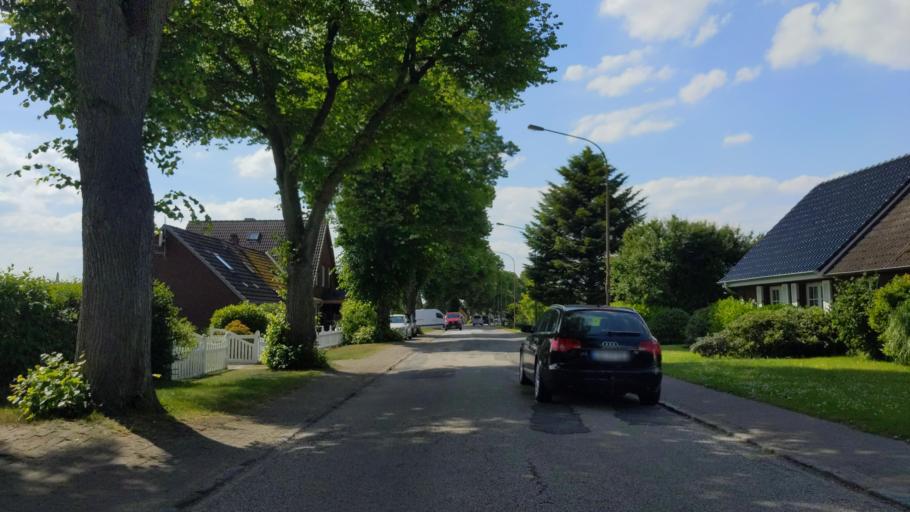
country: DE
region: Schleswig-Holstein
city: Krummesse
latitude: 53.8134
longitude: 10.6348
